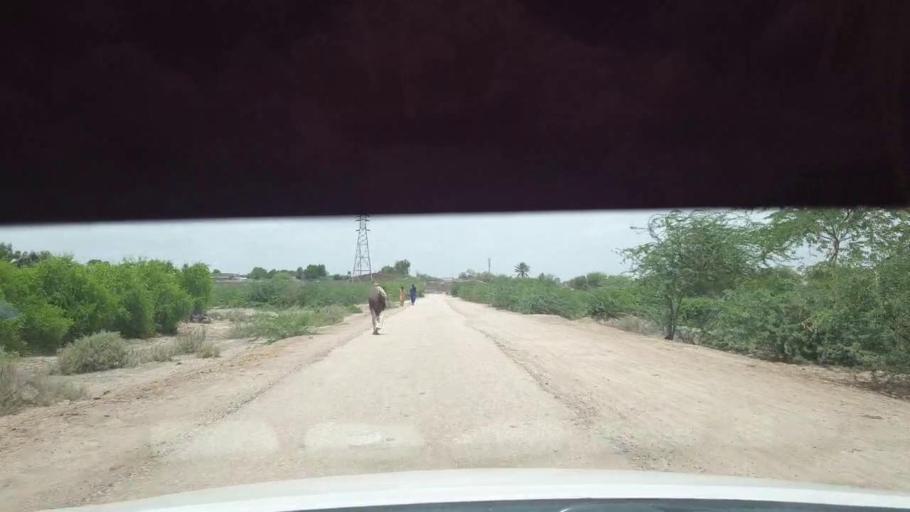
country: PK
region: Sindh
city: Kadhan
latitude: 24.4818
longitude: 68.9937
